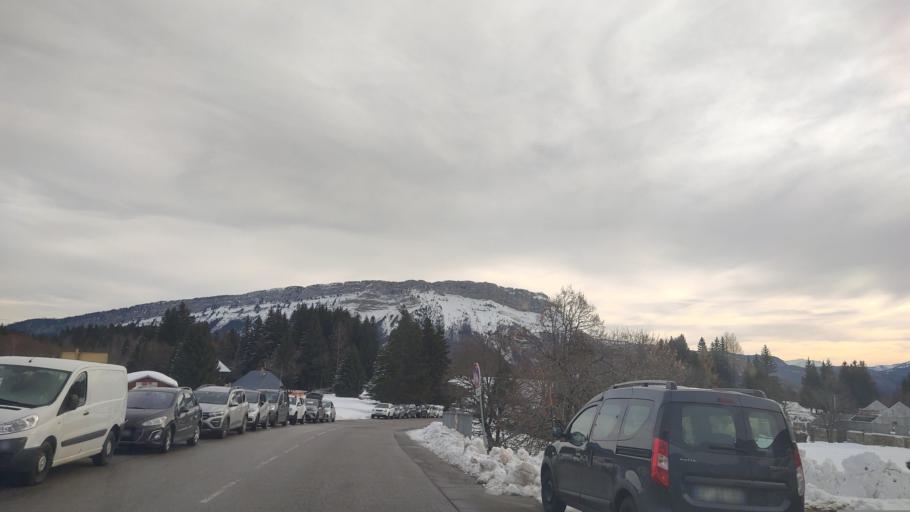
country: FR
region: Rhone-Alpes
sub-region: Departement de la Savoie
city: Mery
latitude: 45.6473
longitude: 5.9846
